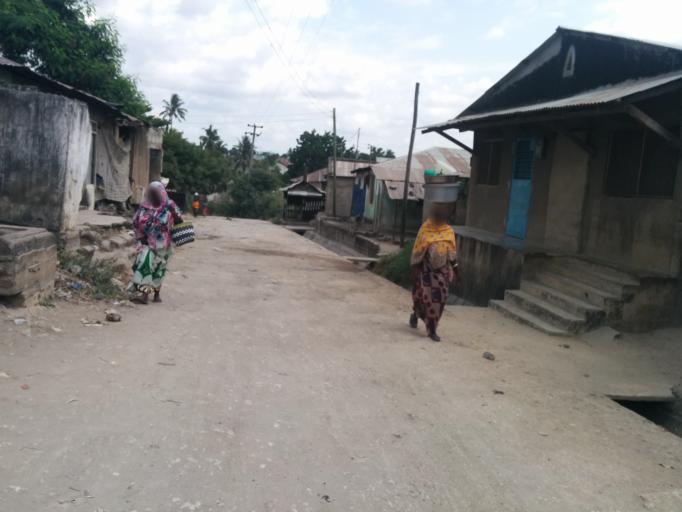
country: TZ
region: Dar es Salaam
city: Dar es Salaam
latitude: -6.8631
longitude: 39.2488
